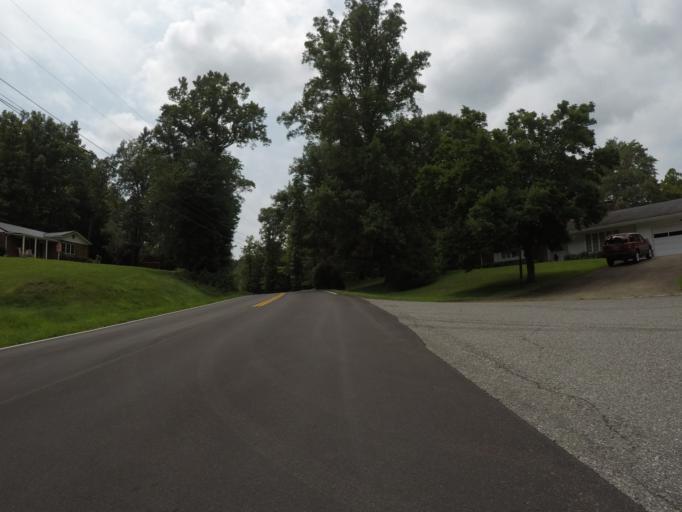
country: US
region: Kentucky
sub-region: Boyd County
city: Catlettsburg
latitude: 38.4300
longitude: -82.6296
